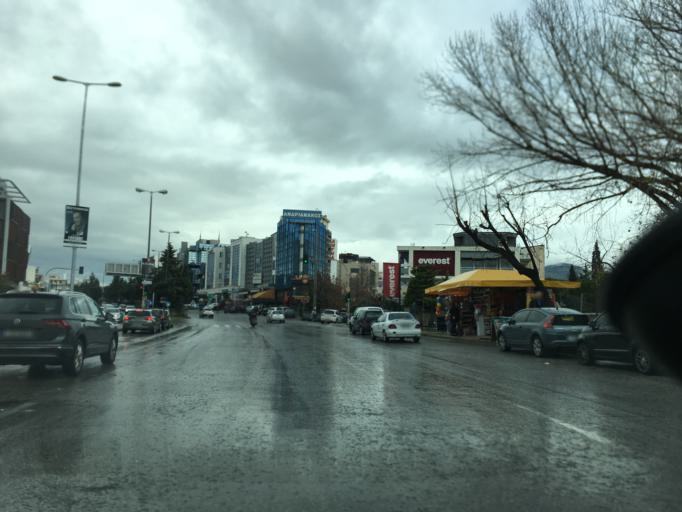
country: GR
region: Attica
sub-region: Nomarchia Athinas
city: Marousi
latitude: 38.0458
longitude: 23.8071
